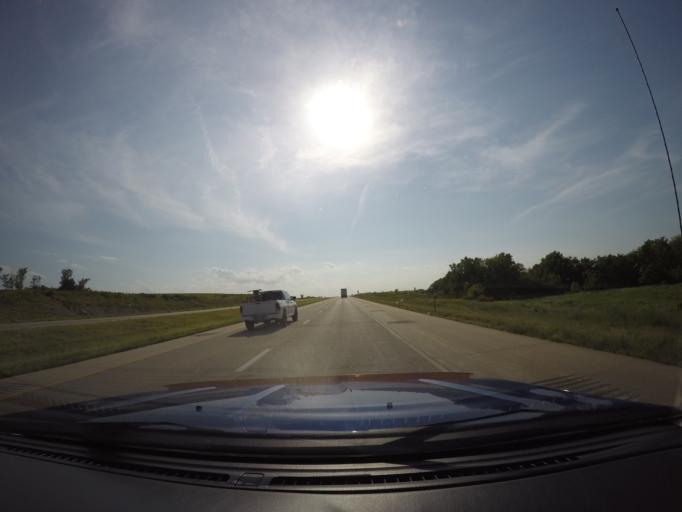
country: US
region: Kansas
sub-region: Wabaunsee County
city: Alma
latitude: 39.0656
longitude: -96.3624
